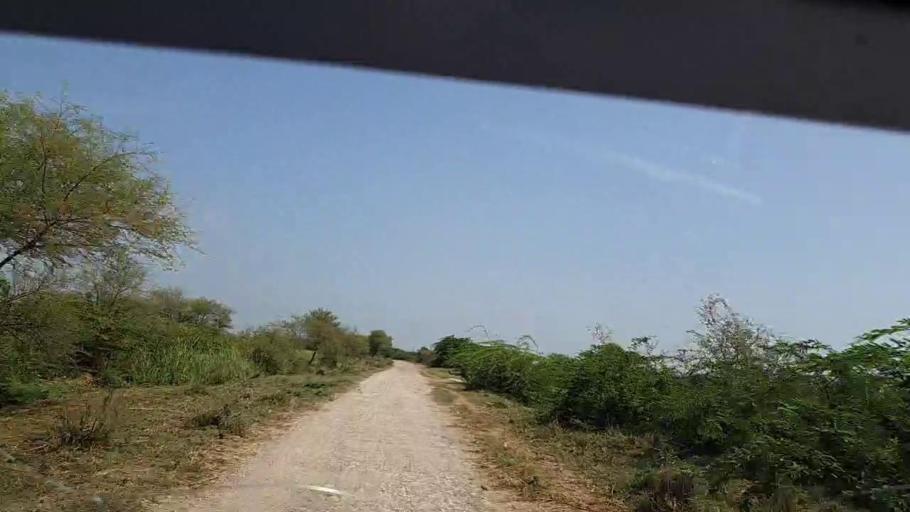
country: PK
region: Sindh
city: Rajo Khanani
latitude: 24.9252
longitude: 68.8715
